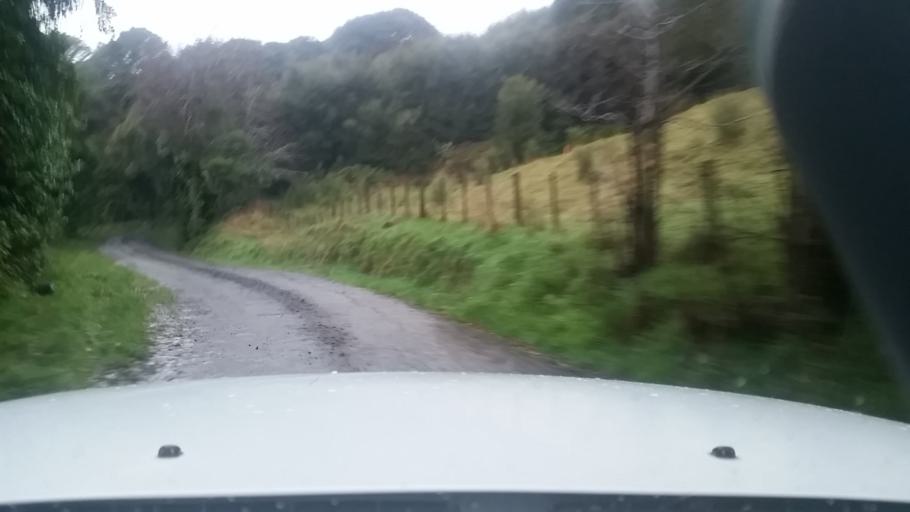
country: NZ
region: Canterbury
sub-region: Christchurch City
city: Christchurch
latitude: -43.8104
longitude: 172.8832
